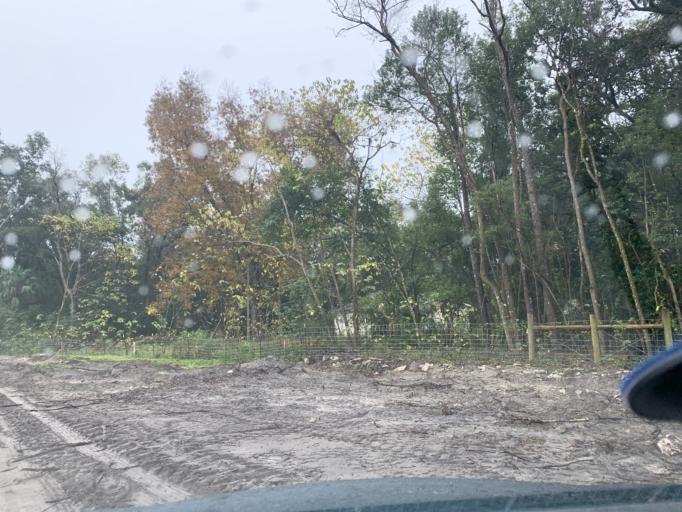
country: US
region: Florida
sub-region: Hernando County
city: Masaryktown
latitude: 28.4519
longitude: -82.4603
